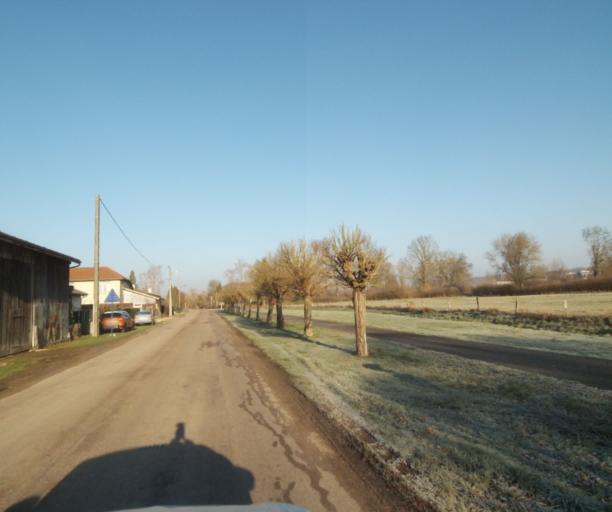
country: FR
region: Champagne-Ardenne
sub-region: Departement de la Haute-Marne
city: Montier-en-Der
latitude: 48.4741
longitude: 4.7639
